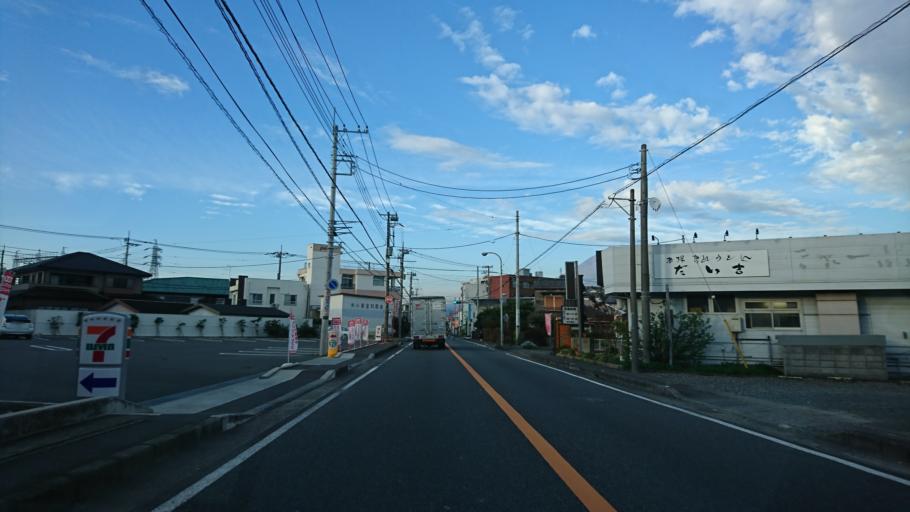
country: JP
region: Shizuoka
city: Fuji
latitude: 35.1471
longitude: 138.6468
